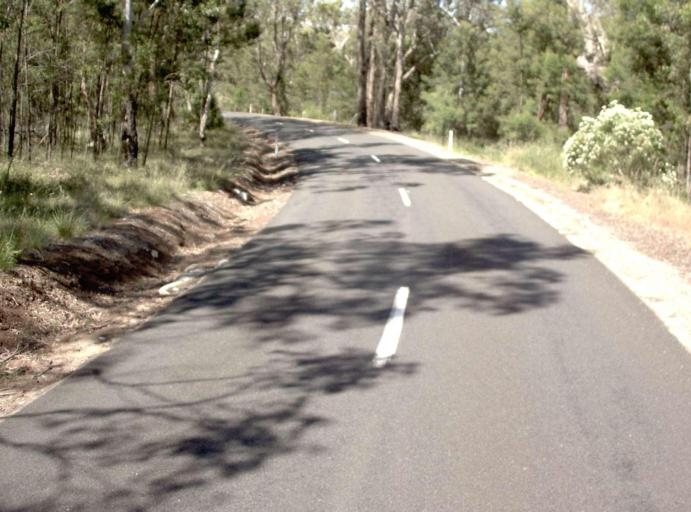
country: AU
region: Victoria
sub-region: East Gippsland
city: Lakes Entrance
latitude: -37.4379
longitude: 148.1912
